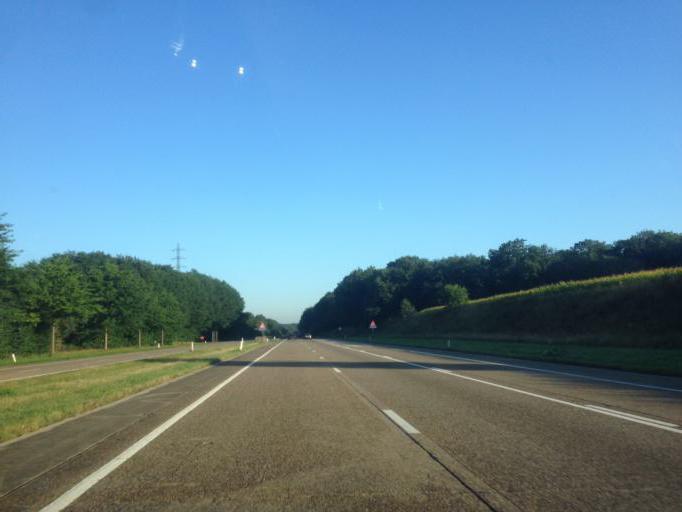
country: BE
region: Flanders
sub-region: Provincie Limburg
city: Overpelt
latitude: 51.1715
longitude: 5.4023
